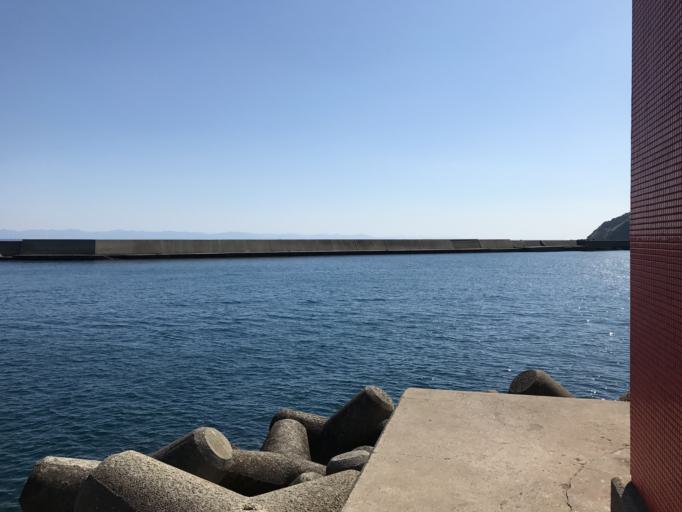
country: JP
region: Nagasaki
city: Nagasaki-shi
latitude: 32.5799
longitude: 129.7856
